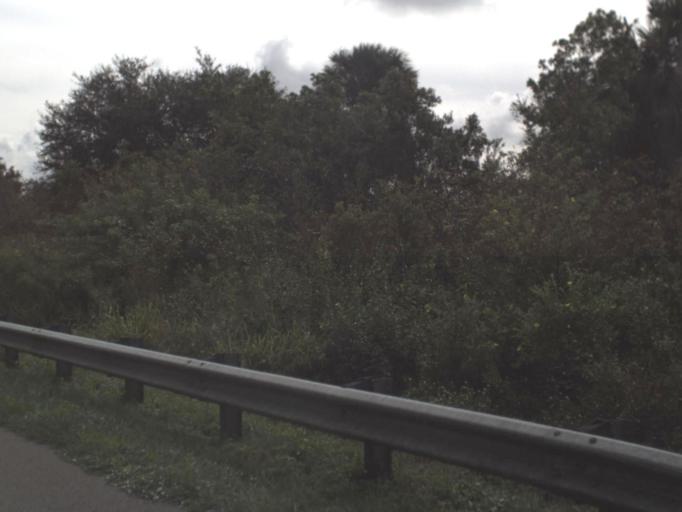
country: US
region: Florida
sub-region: Highlands County
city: Lake Placid
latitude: 27.2098
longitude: -81.1402
